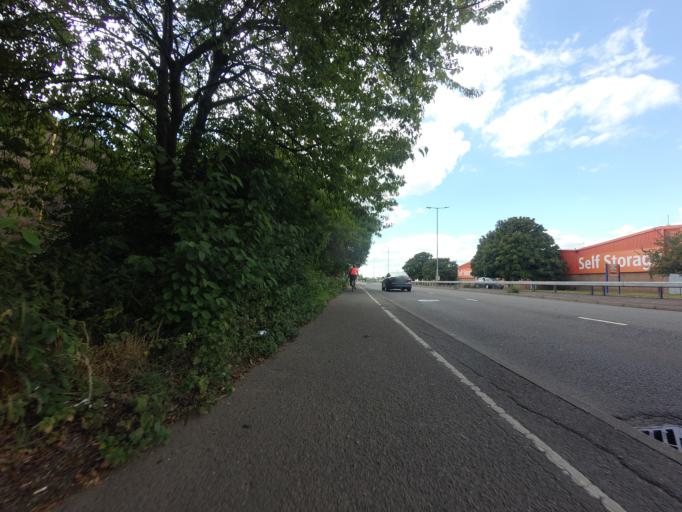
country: GB
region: England
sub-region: East Sussex
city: Eastbourne
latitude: 50.7891
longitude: 0.2997
